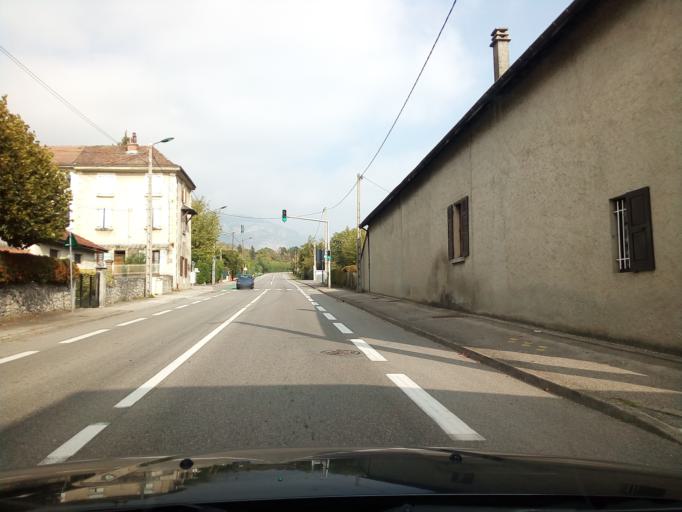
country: FR
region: Rhone-Alpes
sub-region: Departement de l'Isere
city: Saint-Ismier
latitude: 45.2511
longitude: 5.8371
